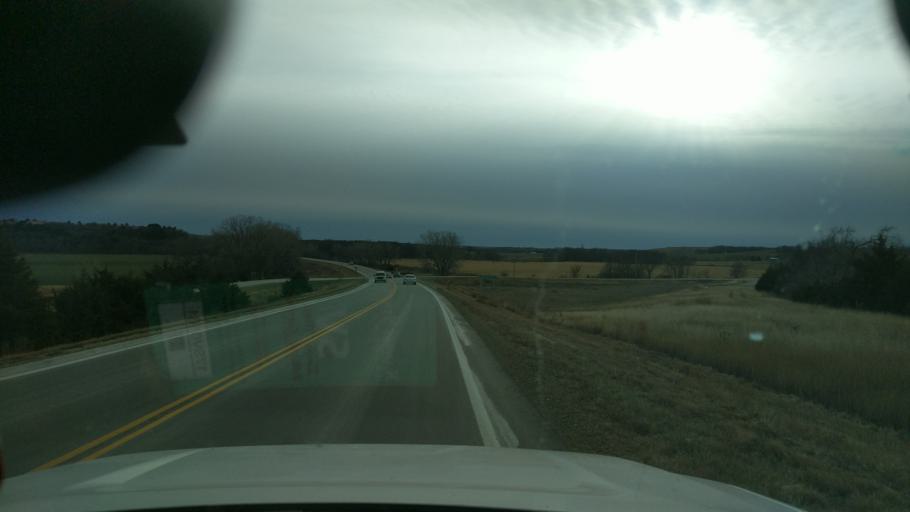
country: US
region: Kansas
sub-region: Geary County
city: Junction City
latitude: 38.9573
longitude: -96.8571
